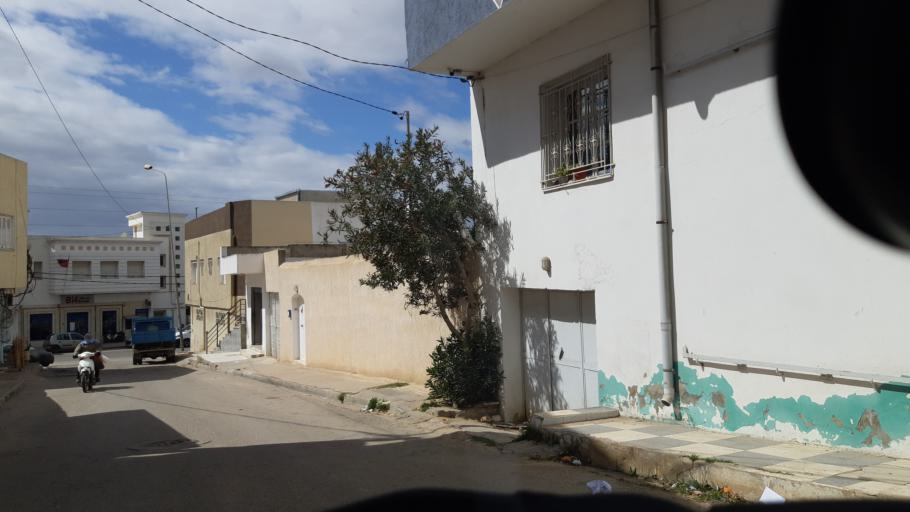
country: TN
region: Susah
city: Akouda
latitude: 35.8754
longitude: 10.5437
